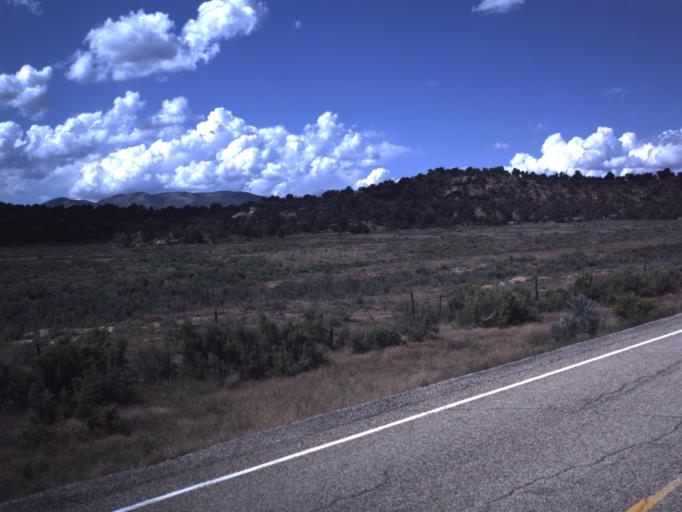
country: US
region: Utah
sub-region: Duchesne County
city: Duchesne
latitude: 40.2380
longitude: -110.7162
